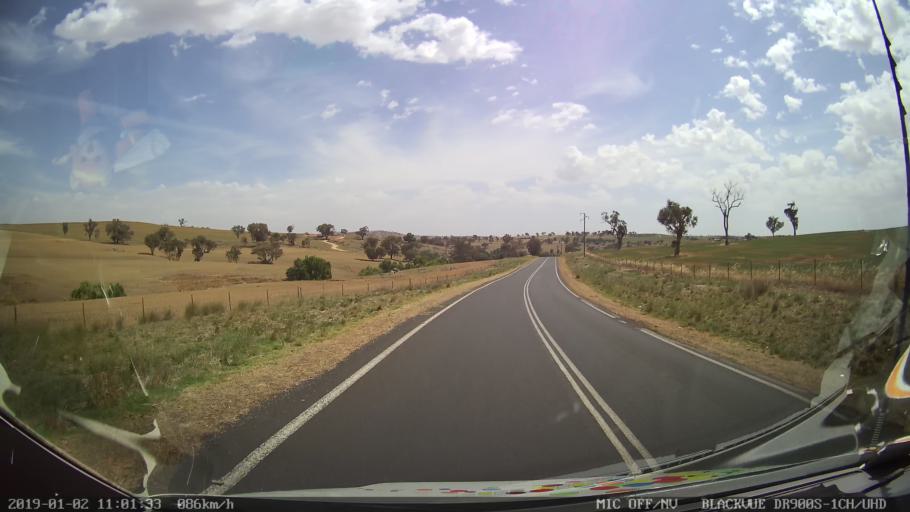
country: AU
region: New South Wales
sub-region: Young
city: Young
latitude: -34.5967
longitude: 148.3207
